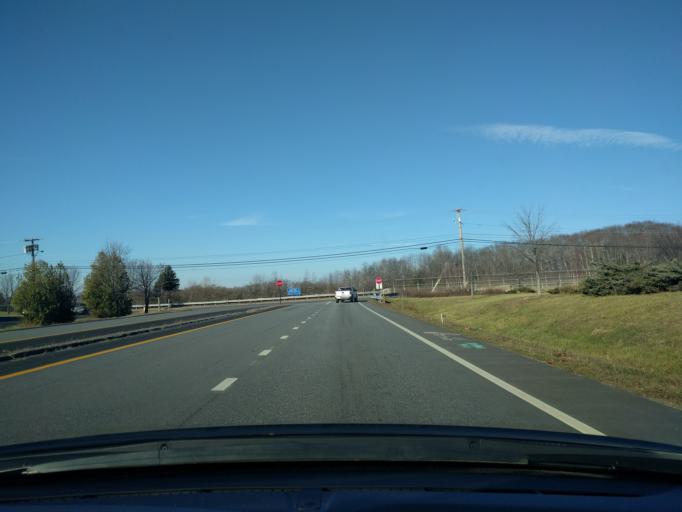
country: US
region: Maine
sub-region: Penobscot County
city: Brewer
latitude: 44.7796
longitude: -68.7591
